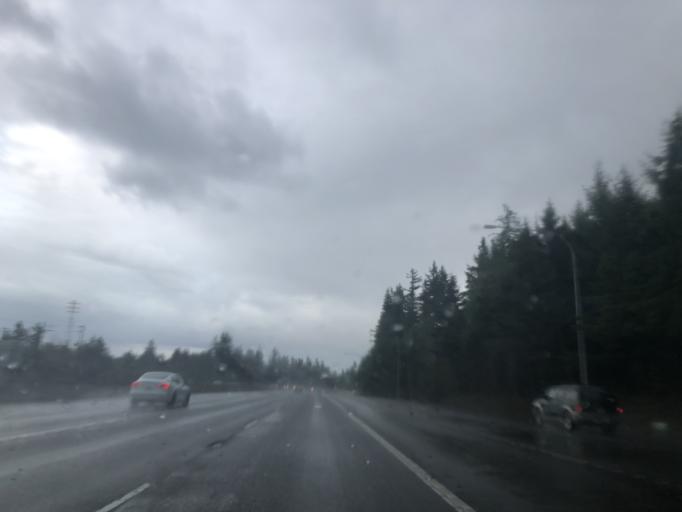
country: US
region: Washington
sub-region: Pierce County
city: Wollochet
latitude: 47.2905
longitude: -122.5636
